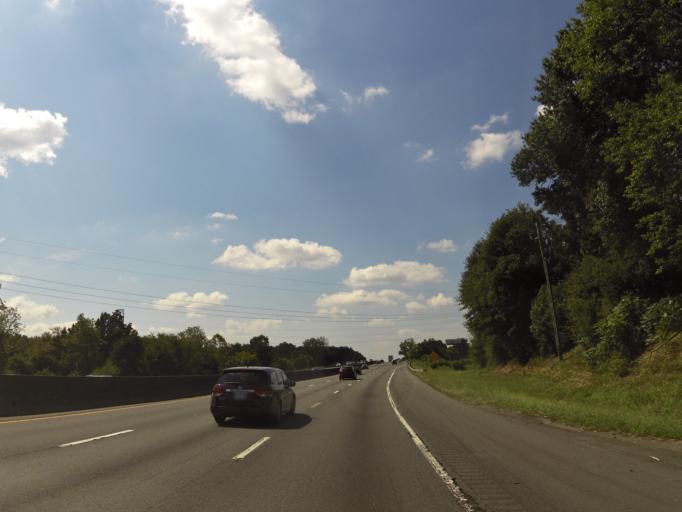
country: US
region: North Carolina
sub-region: Gaston County
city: Gastonia
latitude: 35.2825
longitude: -81.1842
